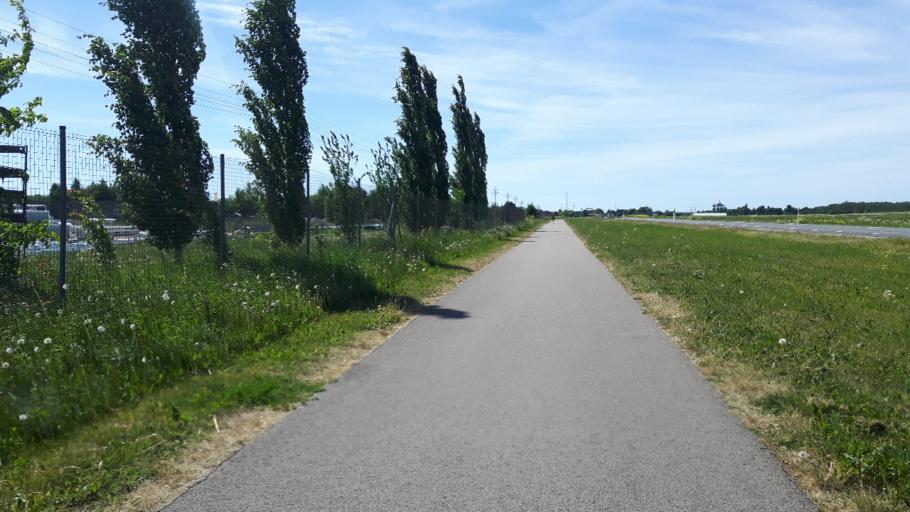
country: EE
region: Harju
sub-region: Kuusalu vald
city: Kuusalu
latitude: 59.4521
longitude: 25.4023
